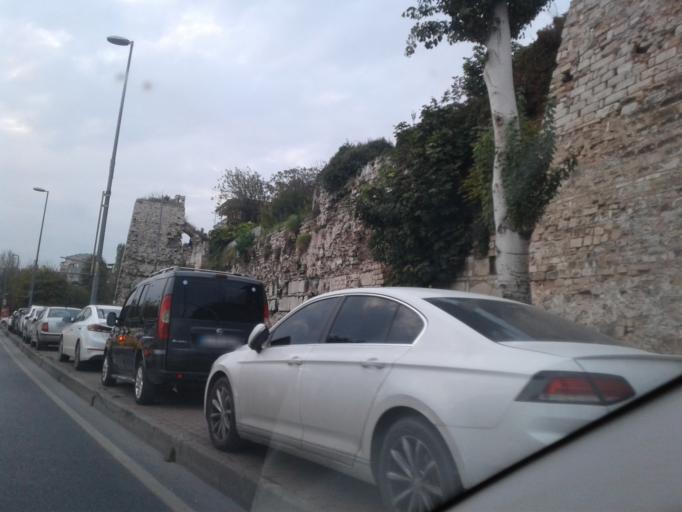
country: TR
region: Istanbul
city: Eminoenue
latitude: 41.0021
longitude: 28.9781
